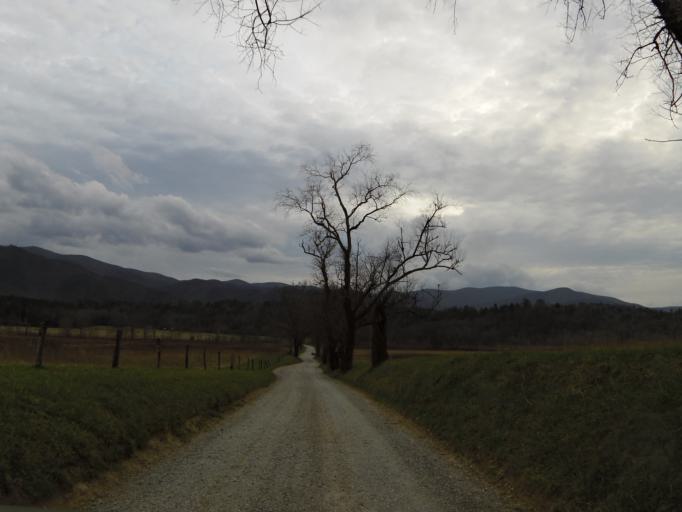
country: US
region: Tennessee
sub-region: Blount County
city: Wildwood
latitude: 35.5970
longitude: -83.8240
